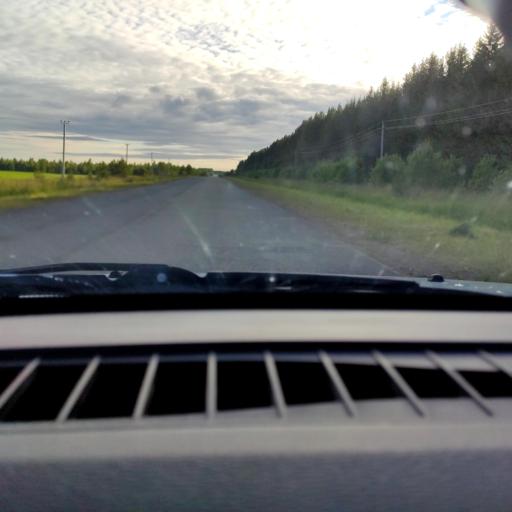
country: RU
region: Perm
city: Uinskoye
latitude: 57.1034
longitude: 56.6567
